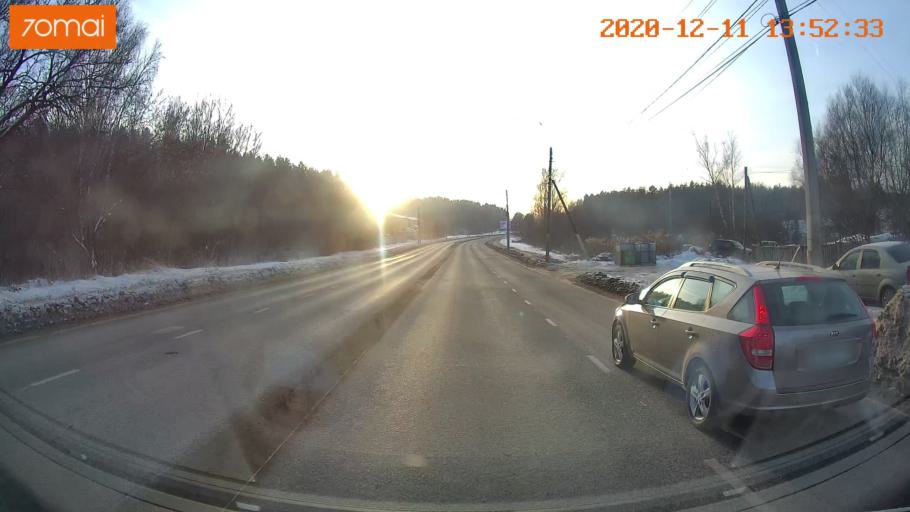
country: RU
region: Kostroma
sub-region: Kostromskoy Rayon
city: Kostroma
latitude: 57.7944
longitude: 40.9752
